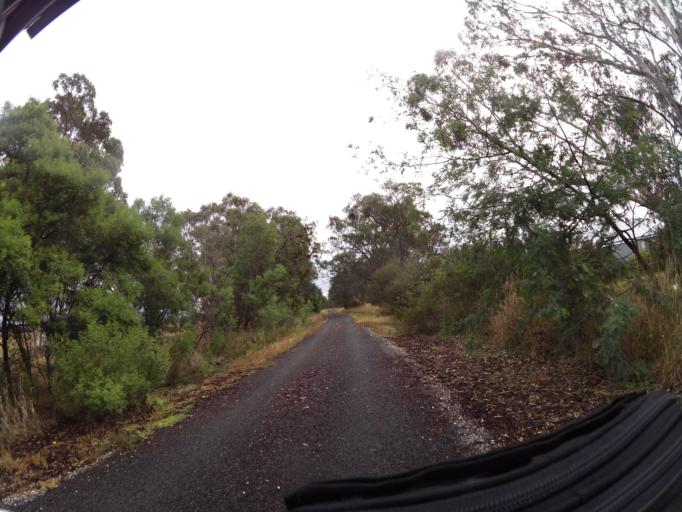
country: AU
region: New South Wales
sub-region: Albury Municipality
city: East Albury
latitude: -36.1397
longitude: 146.9849
